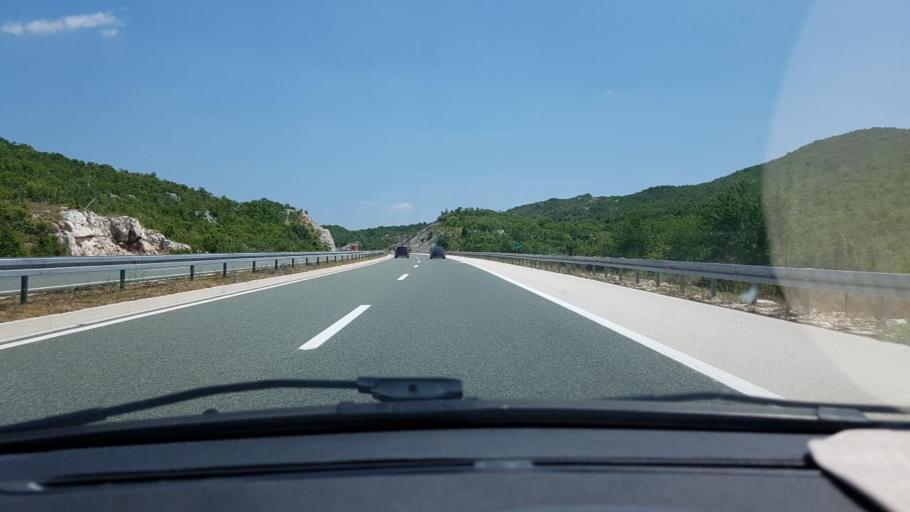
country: HR
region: Splitsko-Dalmatinska
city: Grubine
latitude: 43.3405
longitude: 17.1414
